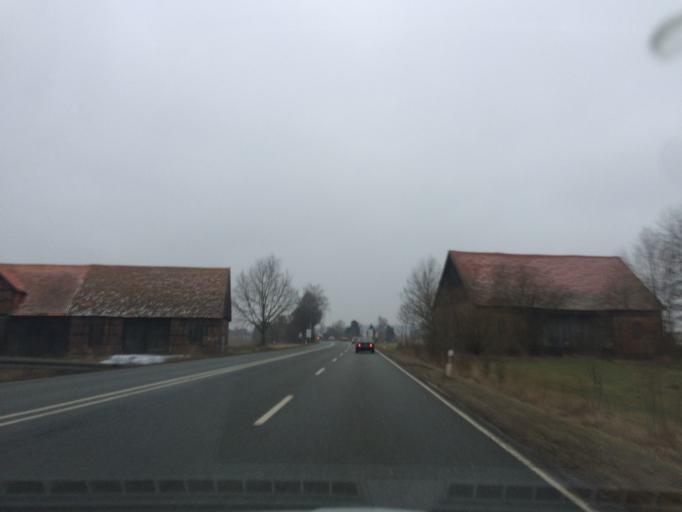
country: DE
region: Hesse
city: Grebenstein
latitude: 51.4247
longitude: 9.4363
